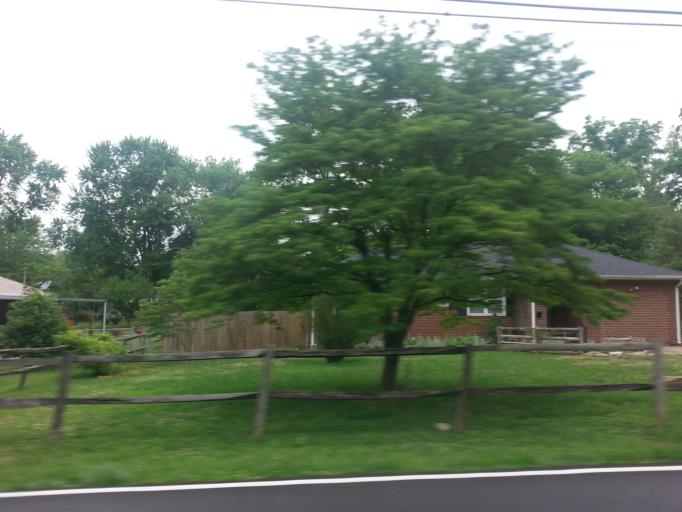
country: US
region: Tennessee
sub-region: Knox County
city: Knoxville
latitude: 36.0199
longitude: -83.9377
